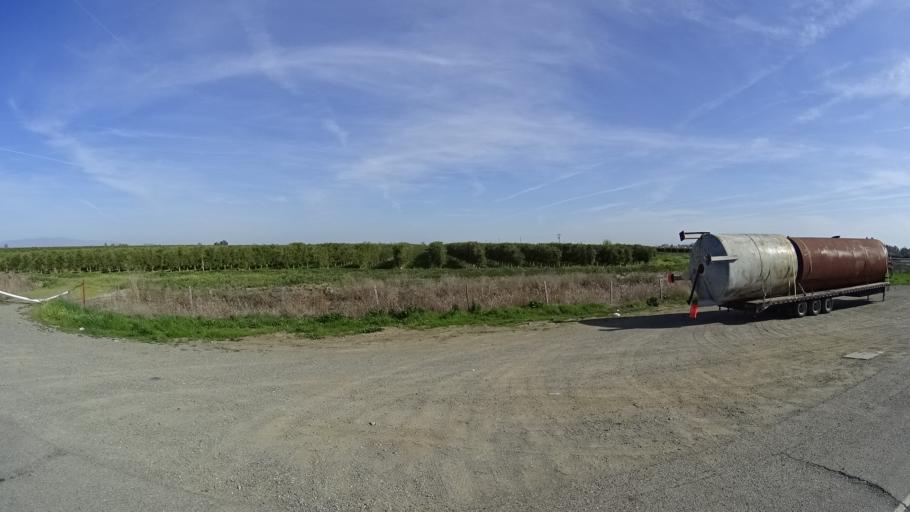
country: US
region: California
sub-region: Glenn County
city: Willows
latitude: 39.6243
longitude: -122.2076
